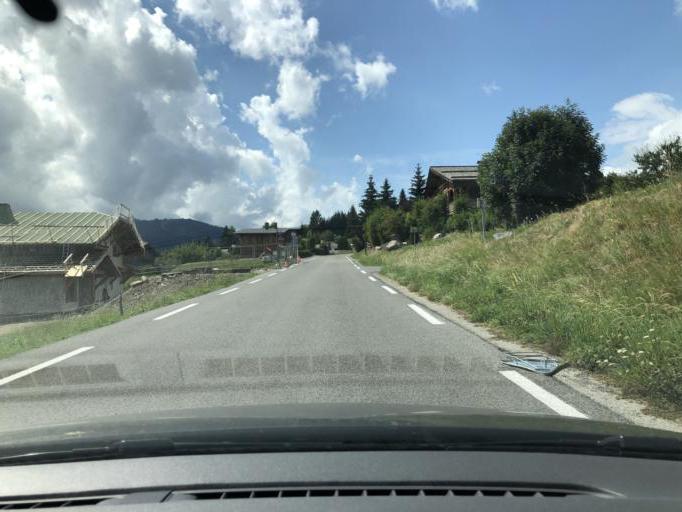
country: FR
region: Rhone-Alpes
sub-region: Departement de la Haute-Savoie
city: Combloux
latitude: 45.8826
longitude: 6.6340
